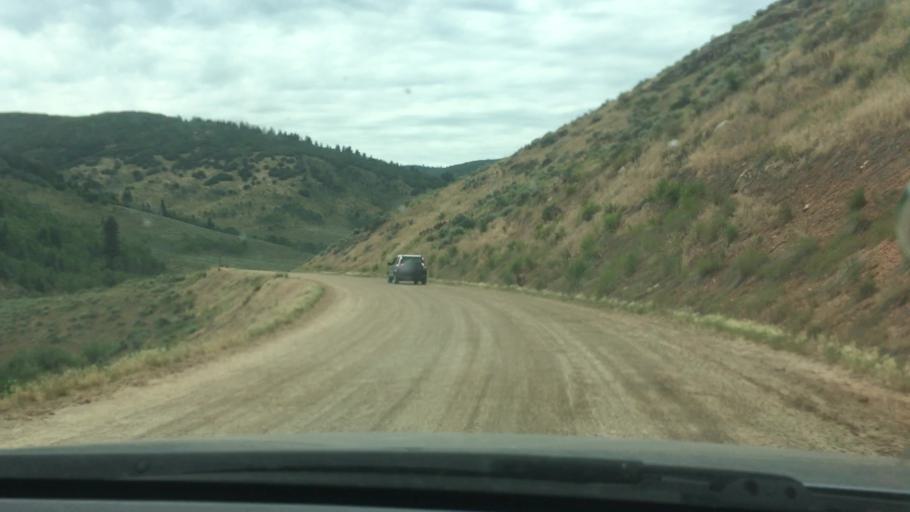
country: US
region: Utah
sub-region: Summit County
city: Summit Park
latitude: 40.7827
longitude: -111.5921
